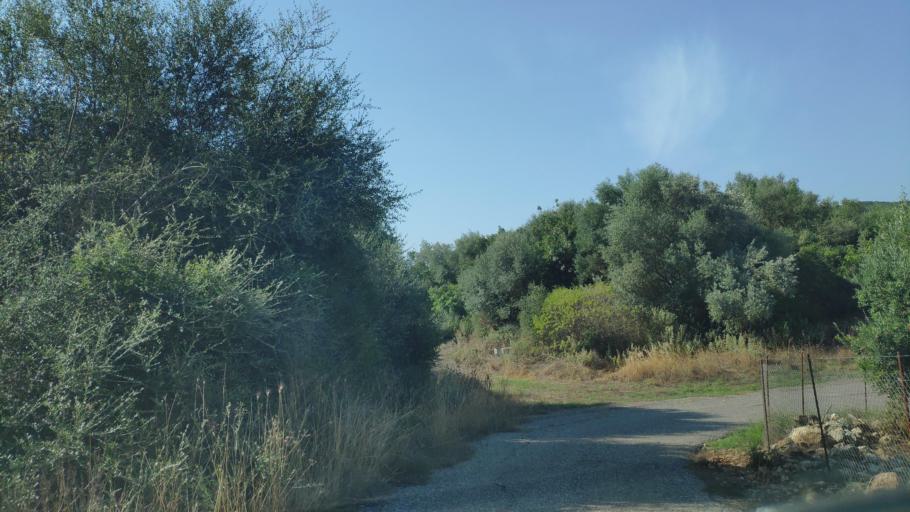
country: GR
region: West Greece
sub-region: Nomos Aitolias kai Akarnanias
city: Fitiai
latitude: 38.6971
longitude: 21.2099
